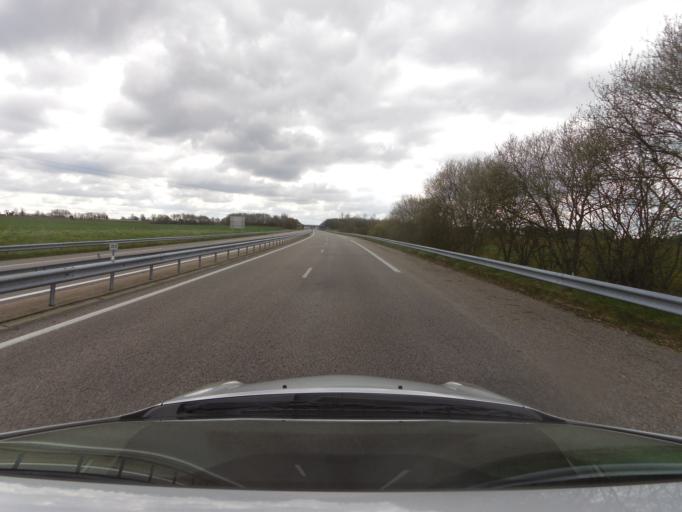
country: FR
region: Haute-Normandie
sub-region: Departement de la Seine-Maritime
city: Etainhus
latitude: 49.5637
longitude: 0.3415
